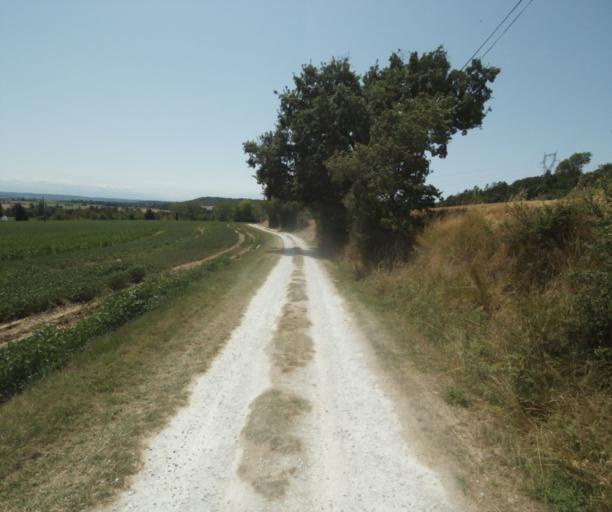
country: FR
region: Midi-Pyrenees
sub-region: Departement de la Haute-Garonne
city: Saint-Felix-Lauragais
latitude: 43.4294
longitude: 1.8882
